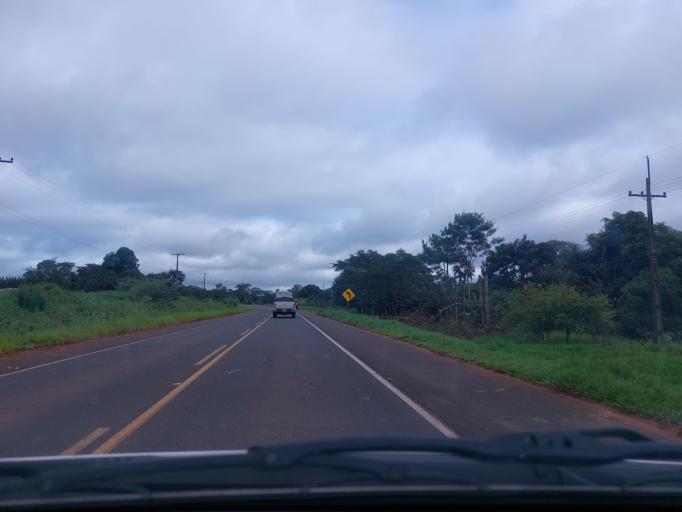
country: PY
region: San Pedro
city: Guayaybi
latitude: -24.6507
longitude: -56.3863
